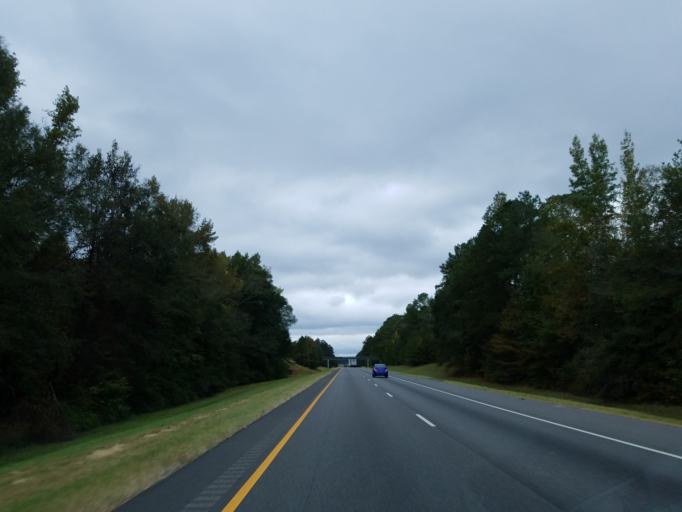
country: US
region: Alabama
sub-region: Hale County
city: Moundville
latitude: 33.0077
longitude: -87.7620
